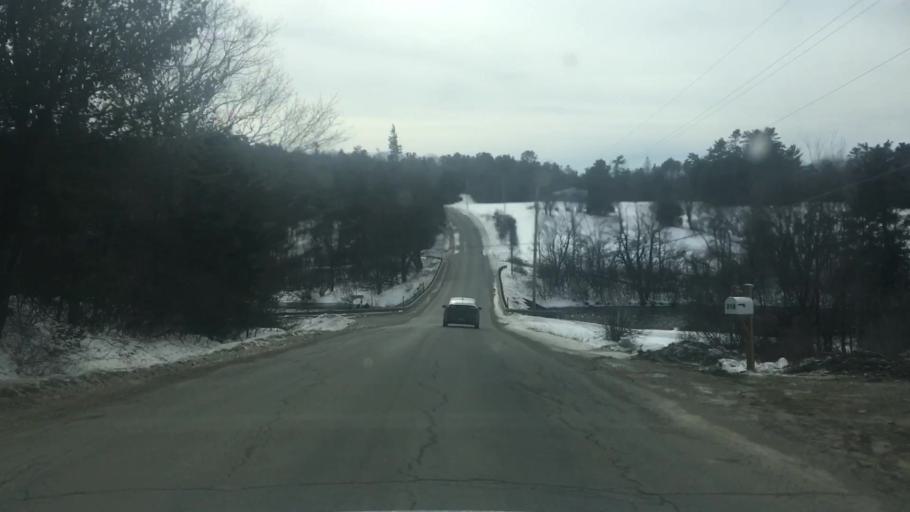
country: US
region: Maine
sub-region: Hancock County
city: Orland
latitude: 44.5944
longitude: -68.7244
